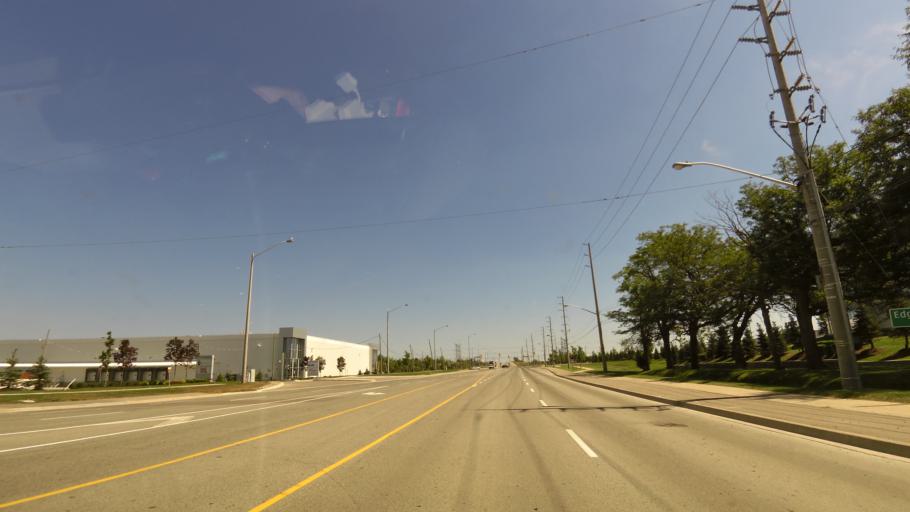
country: CA
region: Ontario
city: Brampton
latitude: 43.6169
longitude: -79.7859
